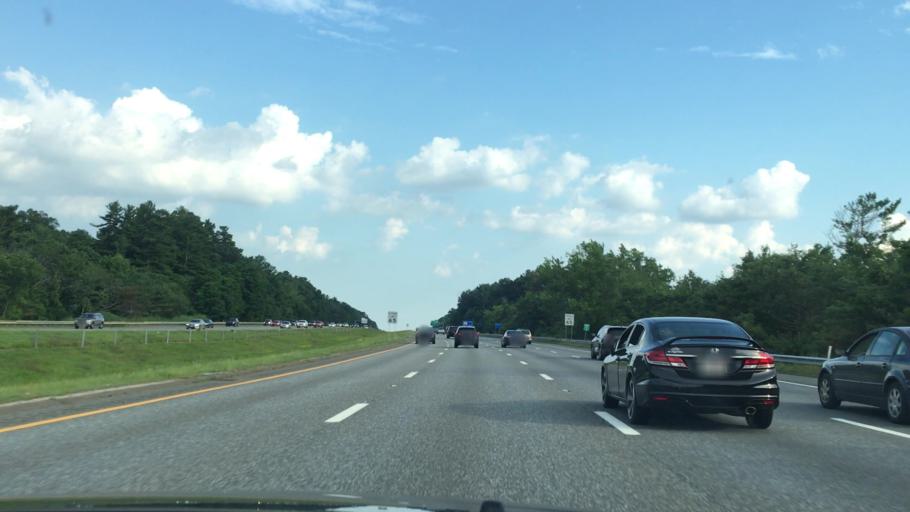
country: US
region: Massachusetts
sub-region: Essex County
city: Topsfield
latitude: 42.6177
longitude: -70.9778
